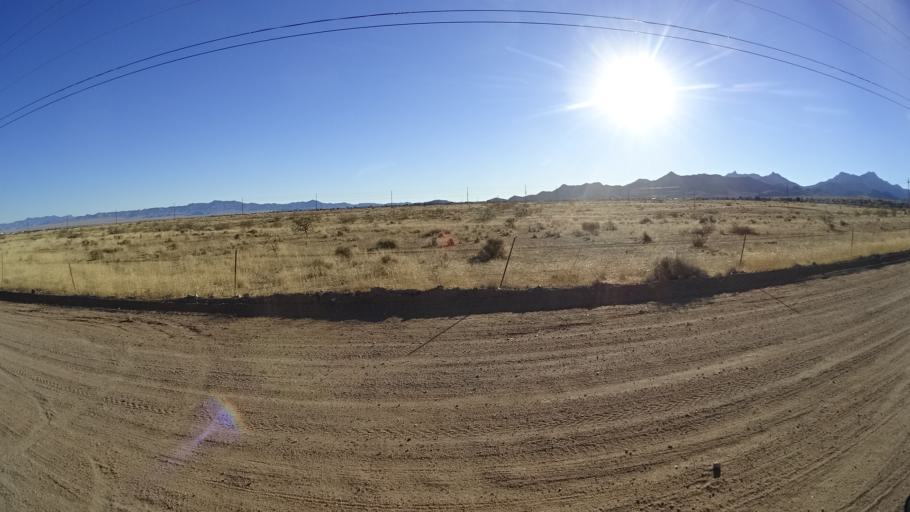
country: US
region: Arizona
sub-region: Mohave County
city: Kingman
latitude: 35.2010
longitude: -113.9940
